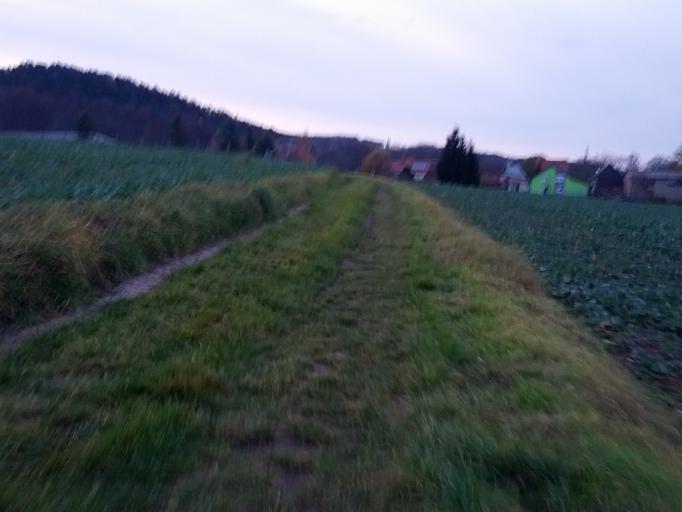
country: DE
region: Thuringia
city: Thal
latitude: 50.9620
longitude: 10.3668
